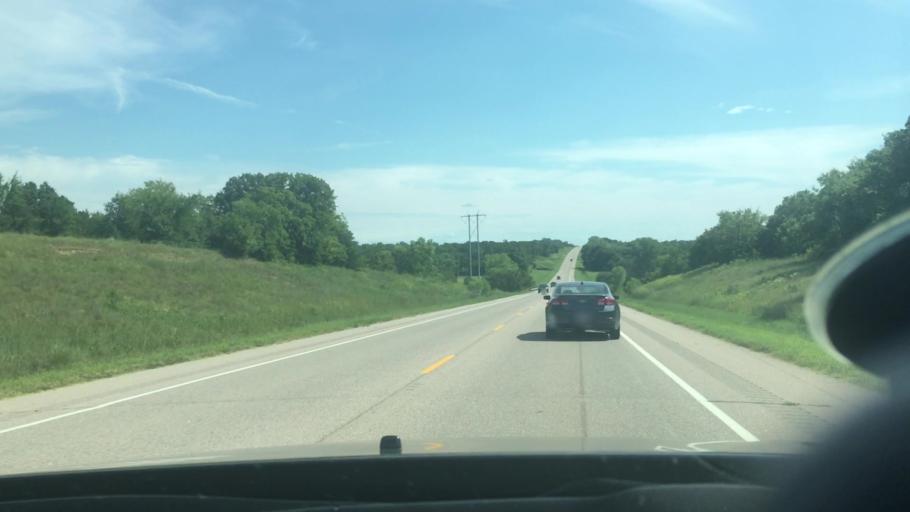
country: US
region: Oklahoma
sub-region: Seminole County
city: Konawa
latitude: 35.0314
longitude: -96.6783
